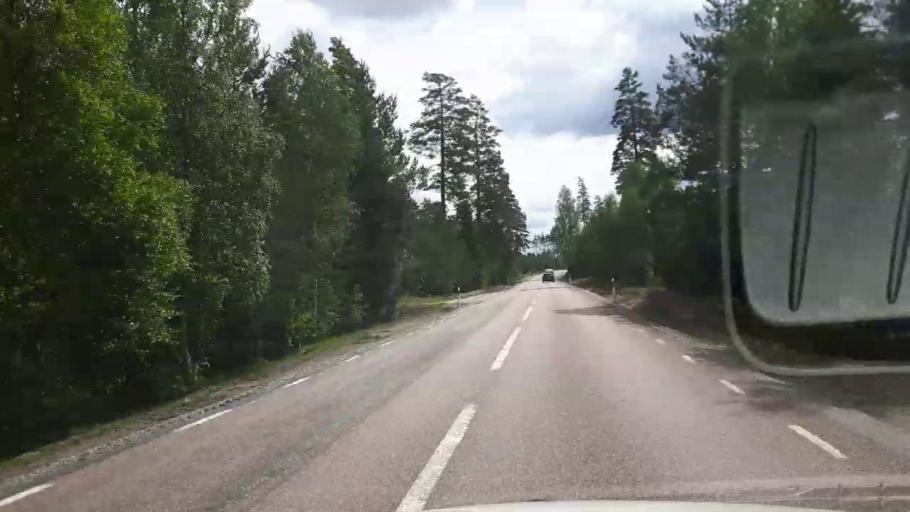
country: SE
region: Vaestmanland
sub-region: Skinnskattebergs Kommun
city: Skinnskatteberg
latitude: 59.8267
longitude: 15.8342
